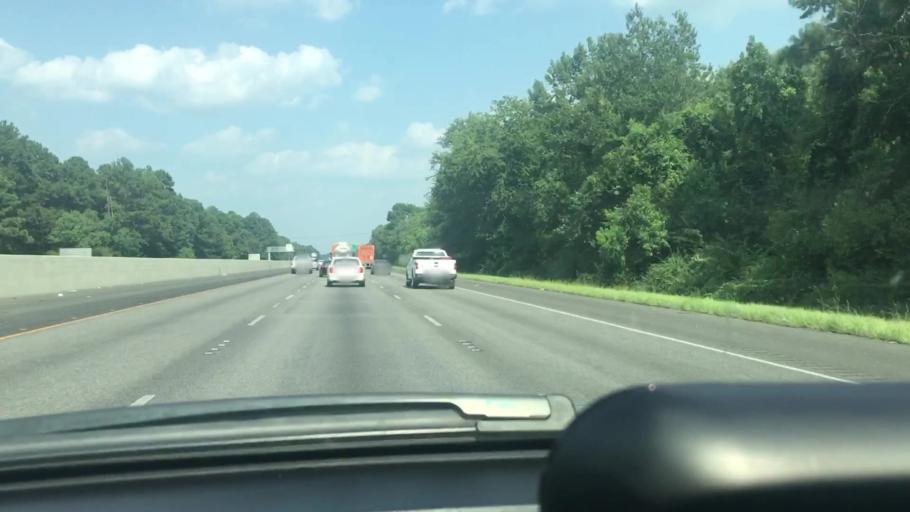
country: US
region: Louisiana
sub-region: Livingston Parish
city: Walker
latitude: 30.4656
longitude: -90.9045
